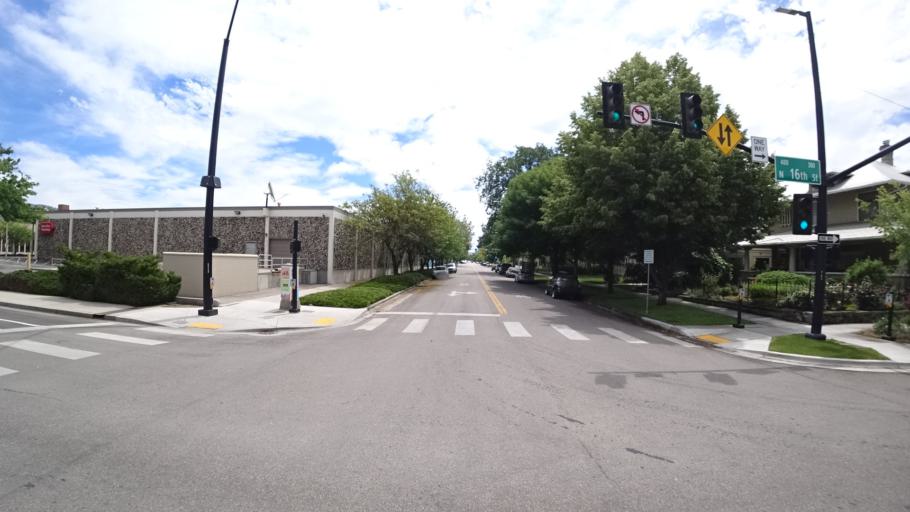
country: US
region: Idaho
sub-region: Ada County
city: Boise
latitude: 43.6227
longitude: -116.2106
